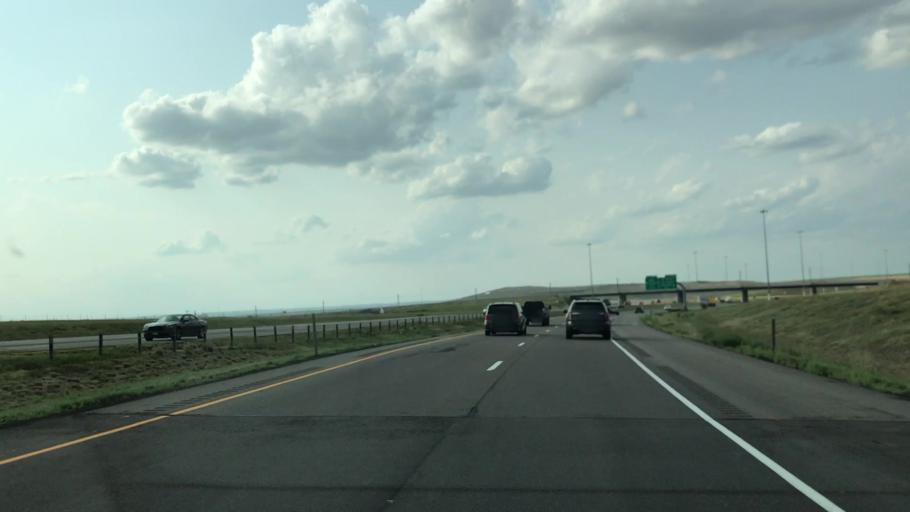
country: US
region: Colorado
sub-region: Adams County
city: Aurora
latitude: 39.8232
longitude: -104.7455
